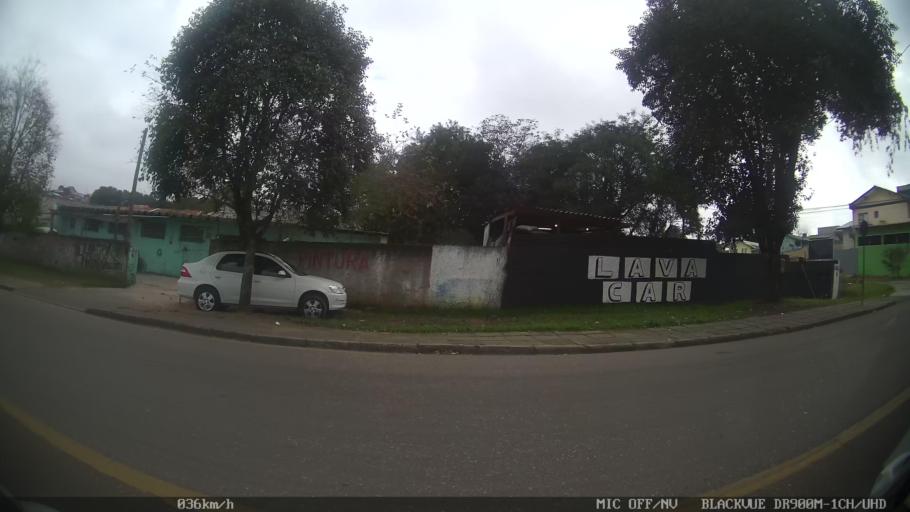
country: BR
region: Parana
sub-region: Curitiba
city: Curitiba
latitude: -25.3683
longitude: -49.2671
